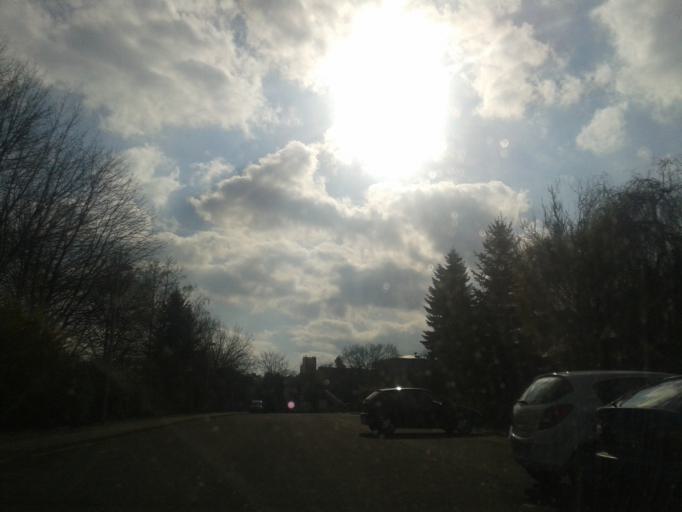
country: DE
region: Saxony
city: Dresden
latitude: 51.0228
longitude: 13.7545
